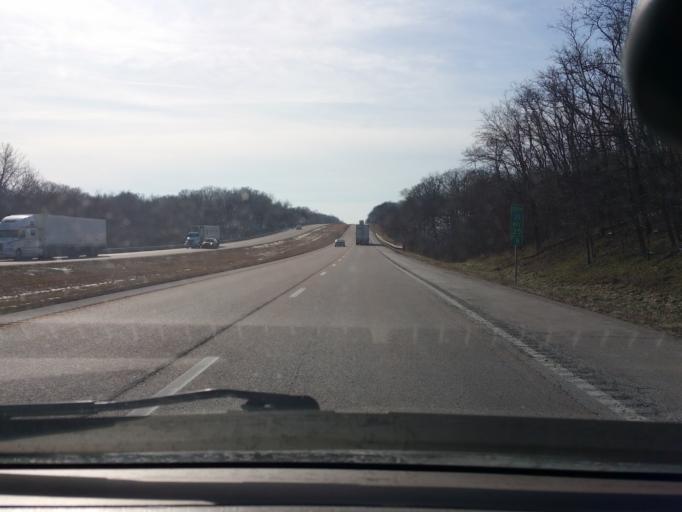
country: US
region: Missouri
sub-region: Clinton County
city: Lathrop
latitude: 39.4932
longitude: -94.3000
